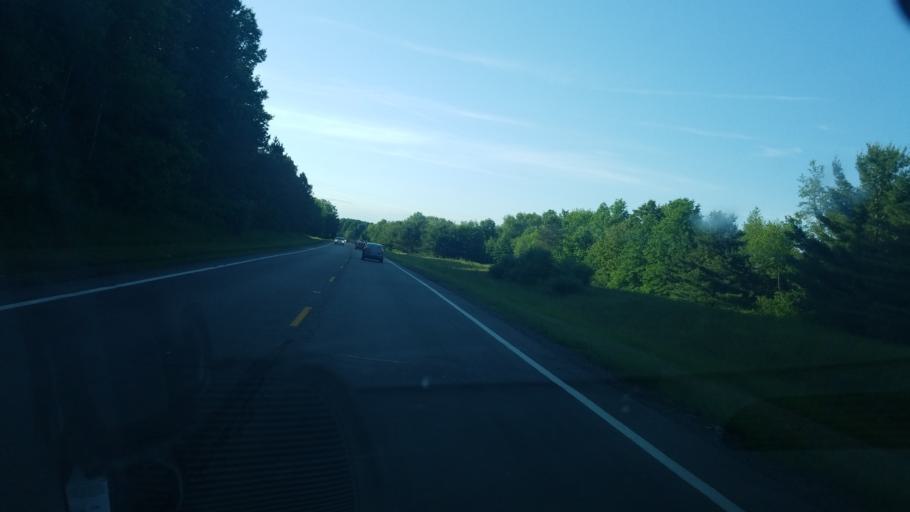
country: US
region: Ohio
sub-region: Portage County
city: Kent
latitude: 41.1502
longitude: -81.3201
